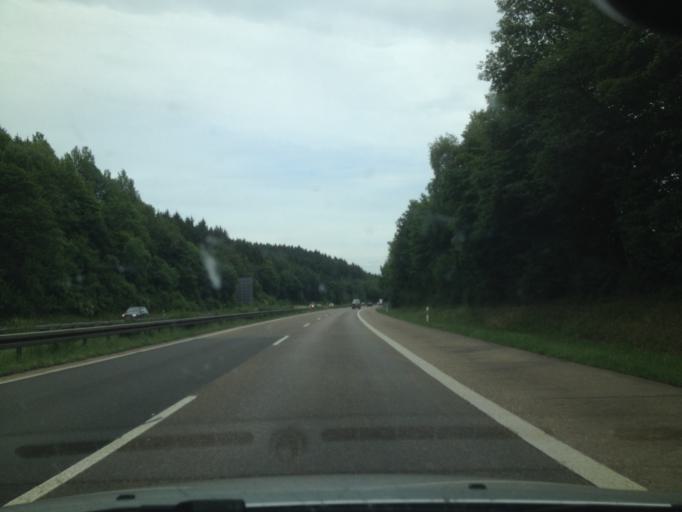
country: DE
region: North Rhine-Westphalia
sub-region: Regierungsbezirk Arnsberg
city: Drolshagen
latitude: 51.0550
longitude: 7.7741
